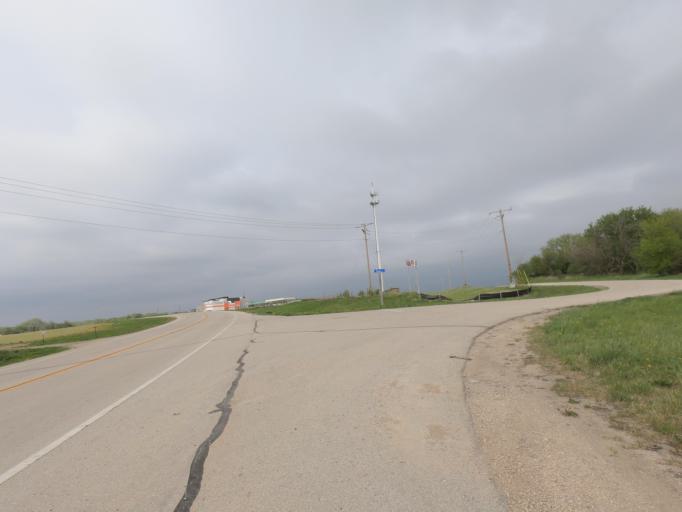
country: US
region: Wisconsin
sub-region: Jefferson County
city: Jefferson
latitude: 43.0318
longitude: -88.8009
